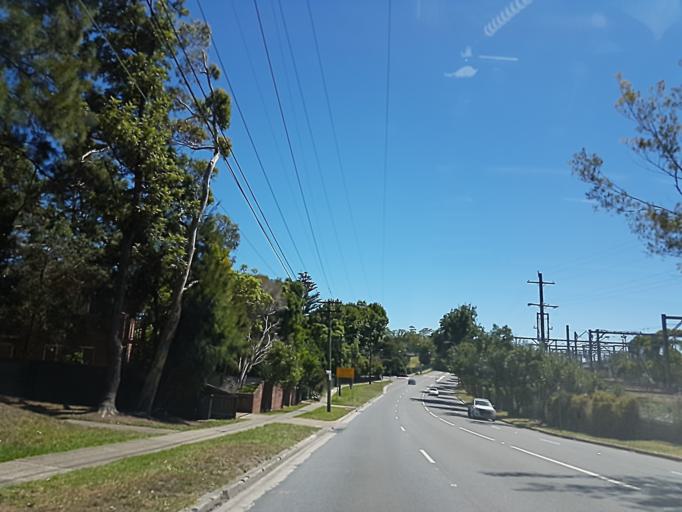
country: AU
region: New South Wales
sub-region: Hornsby Shire
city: Hornsby
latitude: -33.6954
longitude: 151.1005
